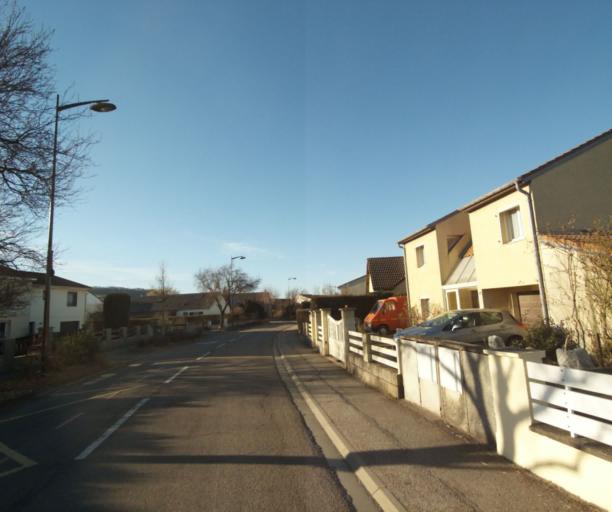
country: FR
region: Lorraine
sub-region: Departement de Meurthe-et-Moselle
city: Pulnoy
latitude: 48.7075
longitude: 6.2555
